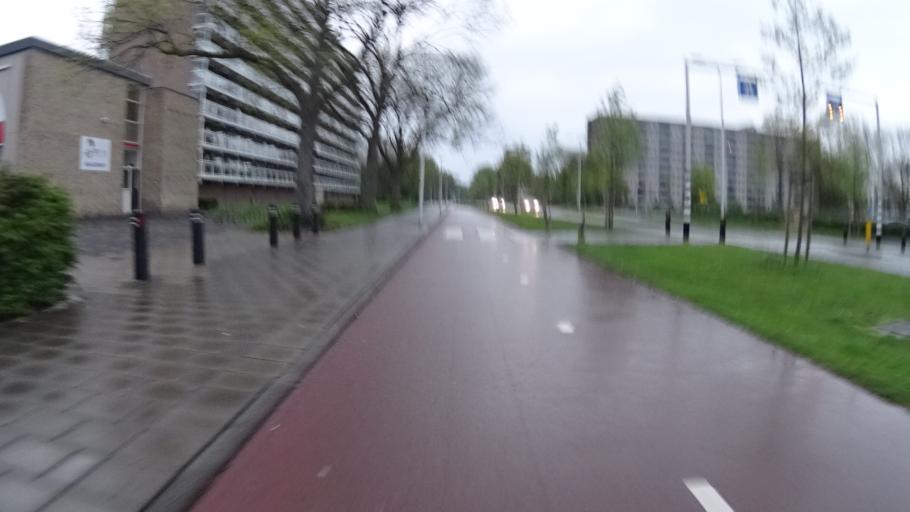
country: NL
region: South Holland
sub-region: Gemeente Spijkenisse
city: Spijkenisse
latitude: 51.8555
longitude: 4.3158
